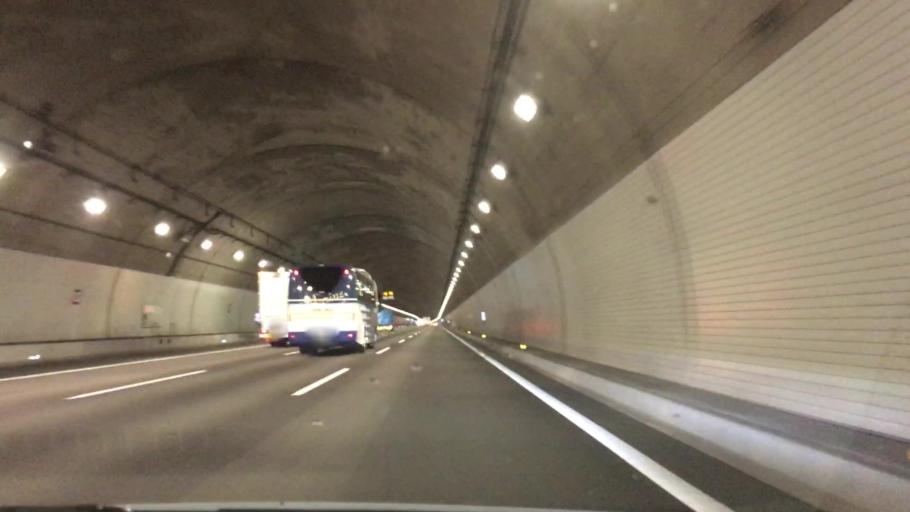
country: JP
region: Shizuoka
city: Fujieda
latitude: 34.9498
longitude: 138.2832
